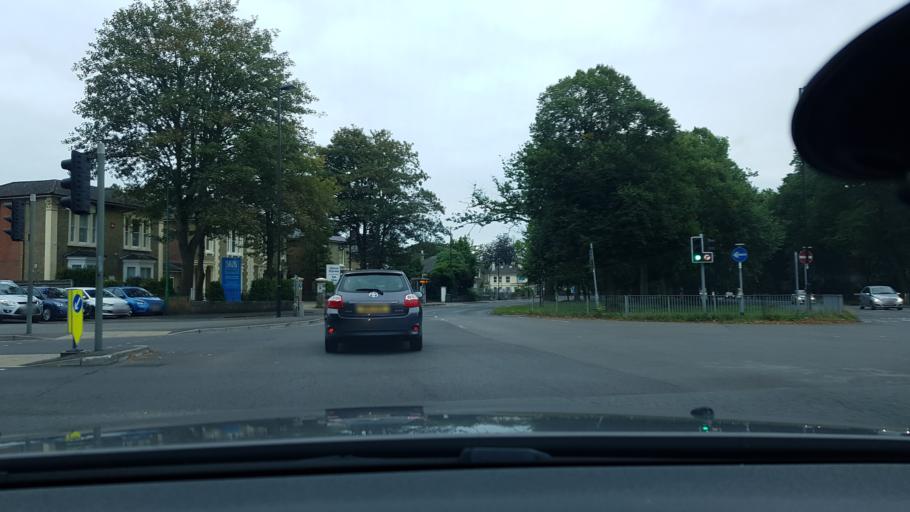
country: GB
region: England
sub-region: Southampton
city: Southampton
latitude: 50.9189
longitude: -1.4039
